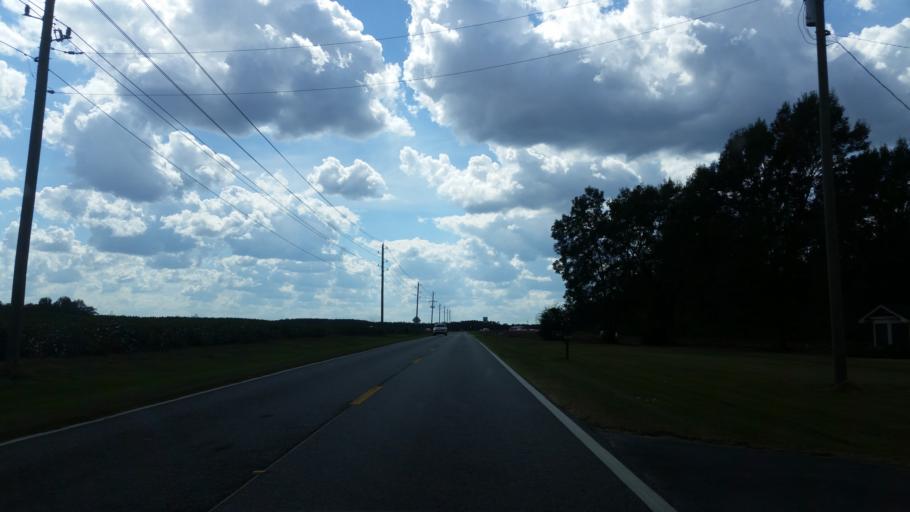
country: US
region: Alabama
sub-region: Escambia County
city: Atmore
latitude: 30.8934
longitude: -87.4775
